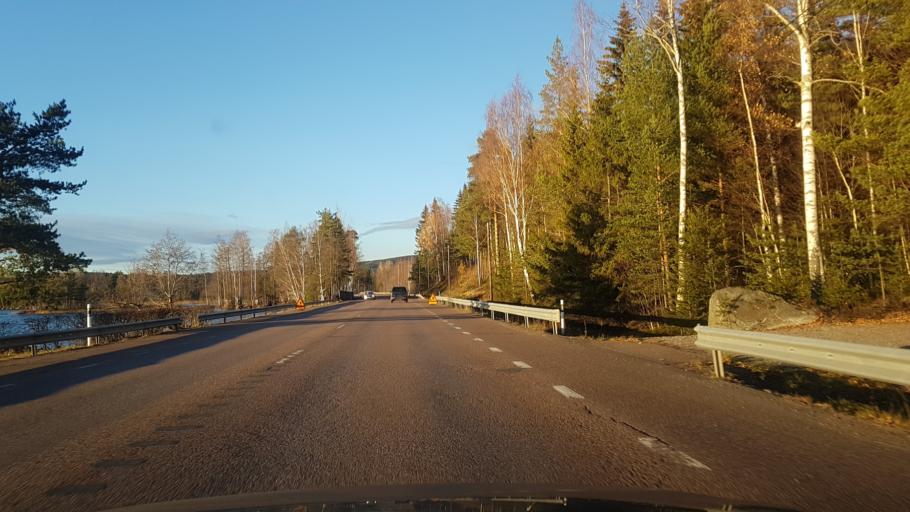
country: SE
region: Dalarna
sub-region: Faluns Kommun
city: Bjursas
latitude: 60.7152
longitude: 15.4602
